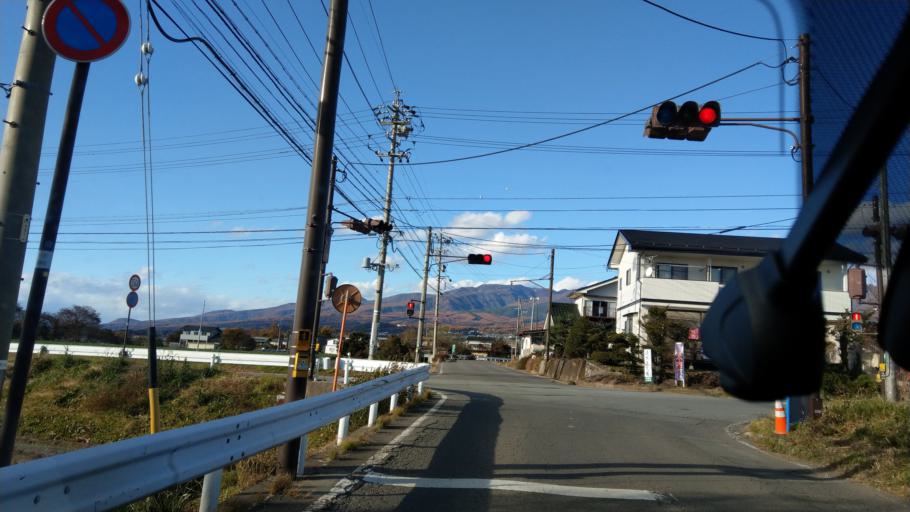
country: JP
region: Nagano
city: Komoro
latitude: 36.3048
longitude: 138.4691
